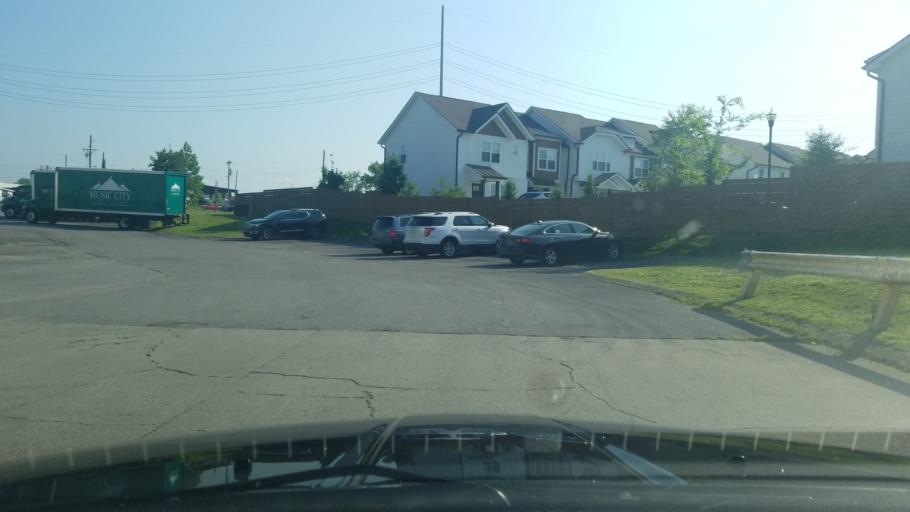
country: US
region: Tennessee
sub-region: Davidson County
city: Belle Meade
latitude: 36.1634
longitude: -86.8585
